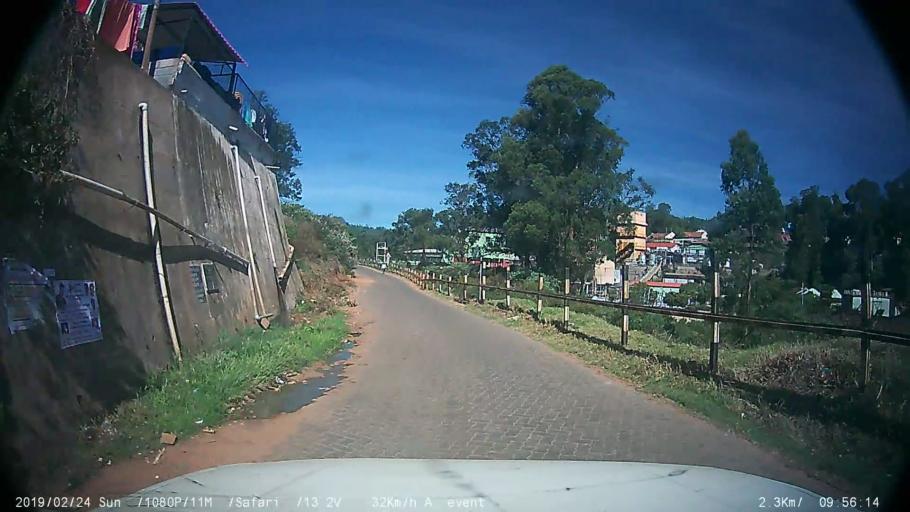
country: IN
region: Tamil Nadu
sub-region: Nilgiri
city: Aravankadu
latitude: 11.3593
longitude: 76.7713
